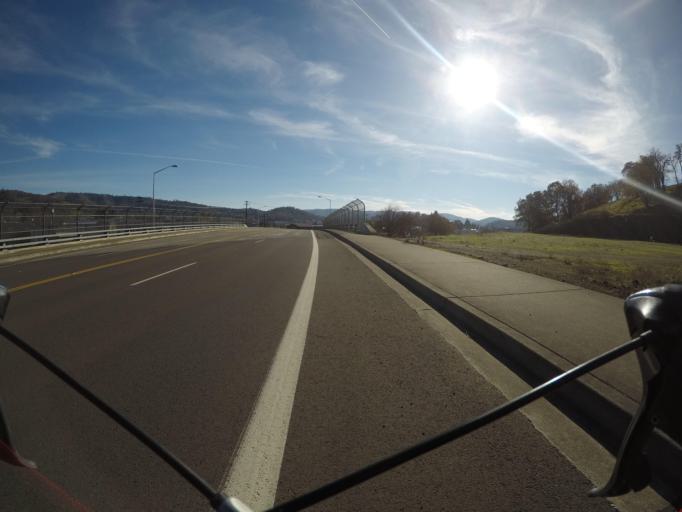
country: US
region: Oregon
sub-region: Douglas County
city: Roseburg
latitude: 43.2369
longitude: -123.3612
